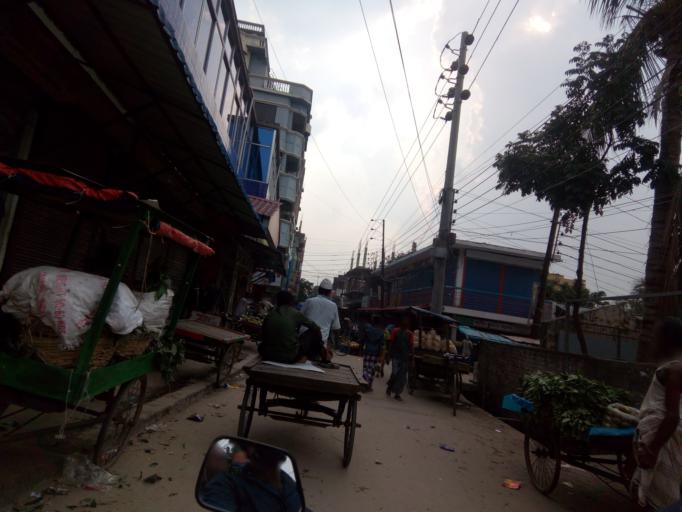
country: BD
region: Dhaka
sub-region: Dhaka
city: Dhaka
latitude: 23.7091
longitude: 90.4599
